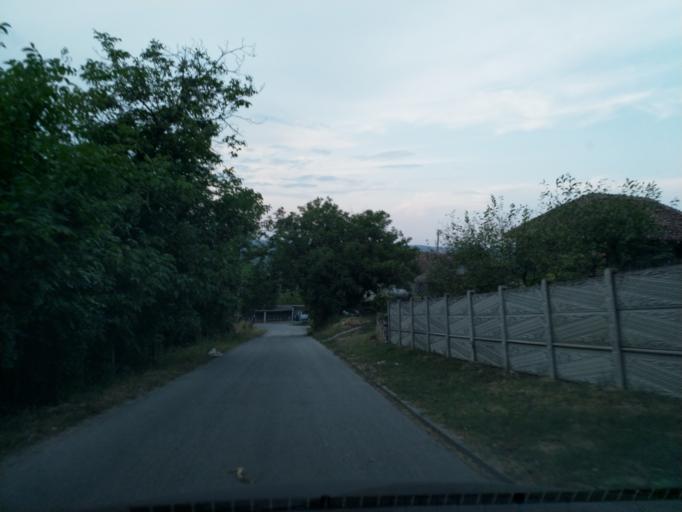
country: RS
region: Central Serbia
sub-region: Pomoravski Okrug
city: Paracin
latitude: 43.8495
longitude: 21.5315
